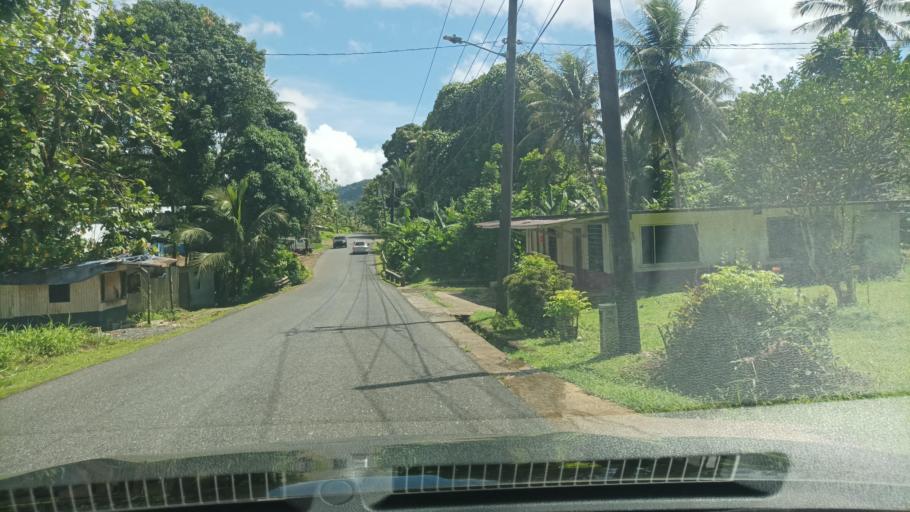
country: FM
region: Pohnpei
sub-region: Sokehs Municipality
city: Palikir - National Government Center
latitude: 6.9318
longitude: 158.1804
